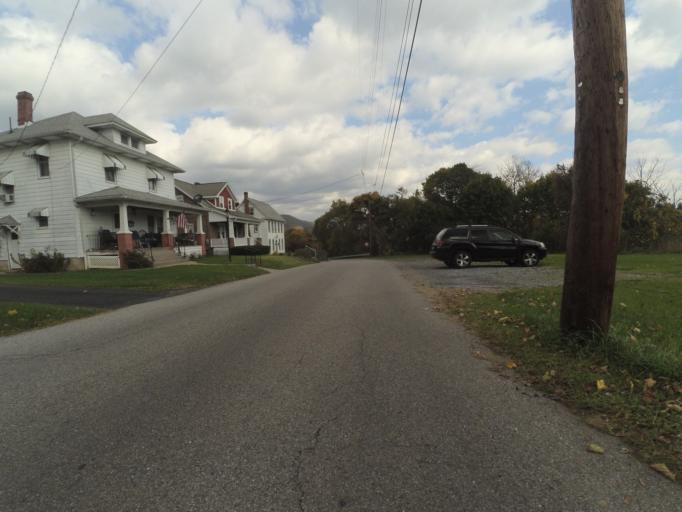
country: US
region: Pennsylvania
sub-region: Centre County
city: Bellefonte
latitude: 40.9106
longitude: -77.7851
